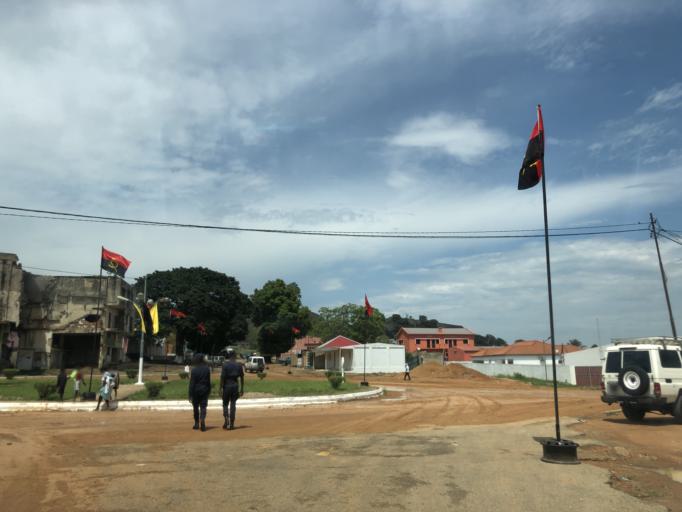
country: AO
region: Cuanza Sul
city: Quibala
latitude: -10.7332
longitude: 14.9799
